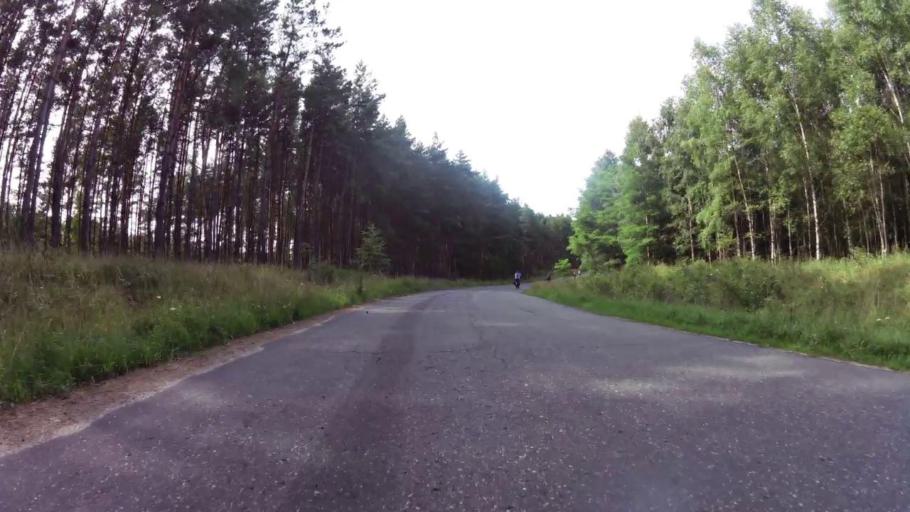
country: PL
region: West Pomeranian Voivodeship
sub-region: Powiat stargardzki
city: Insko
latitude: 53.3809
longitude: 15.5976
